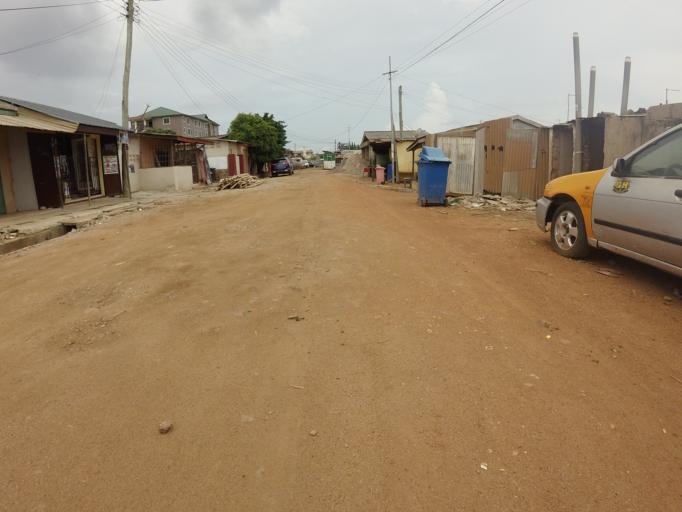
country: GH
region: Greater Accra
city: Accra
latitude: 5.6014
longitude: -0.2203
